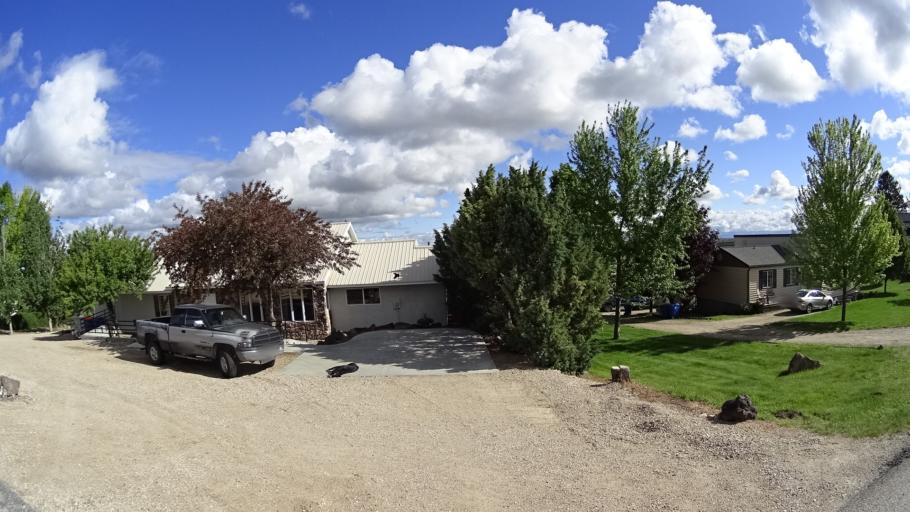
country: US
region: Idaho
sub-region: Ada County
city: Kuna
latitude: 43.4592
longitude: -116.4453
